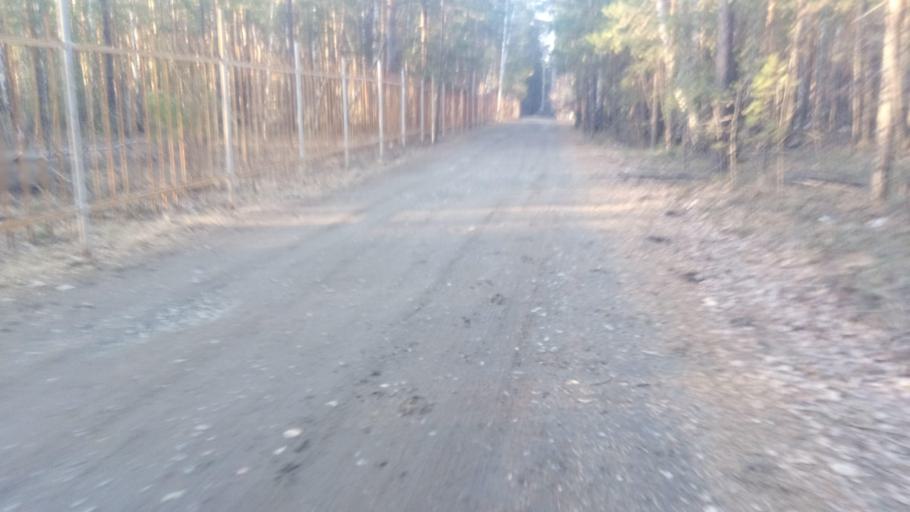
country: RU
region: Chelyabinsk
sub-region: Gorod Chelyabinsk
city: Chelyabinsk
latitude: 55.1278
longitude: 61.3483
